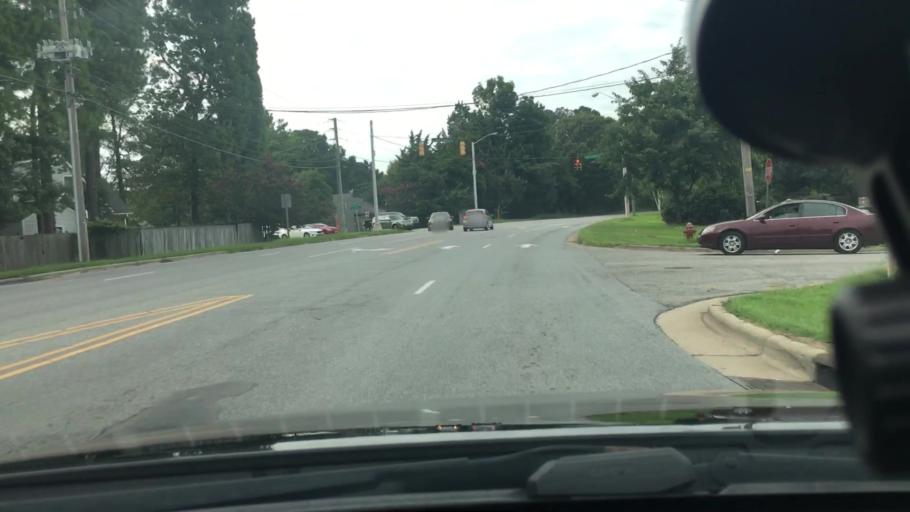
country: US
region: North Carolina
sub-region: Pitt County
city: Greenville
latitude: 35.5859
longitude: -77.3467
